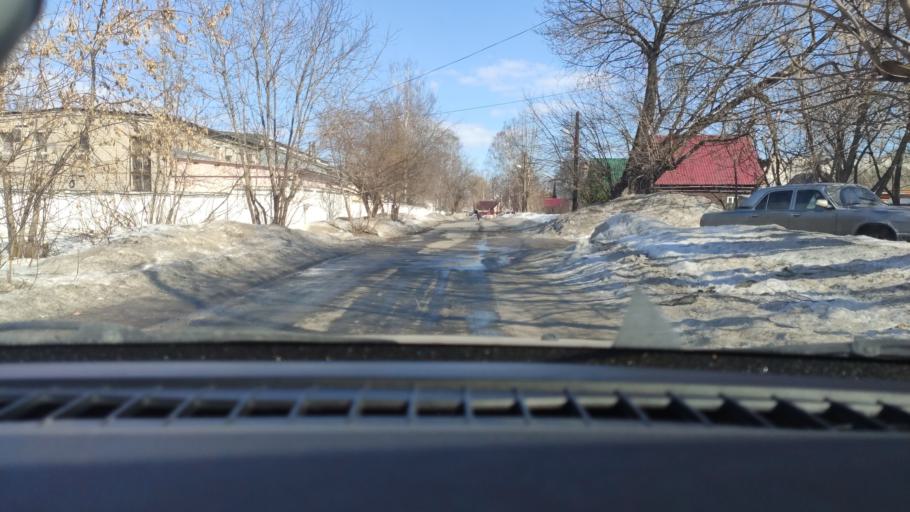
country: RU
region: Perm
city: Polazna
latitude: 58.1287
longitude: 56.3857
